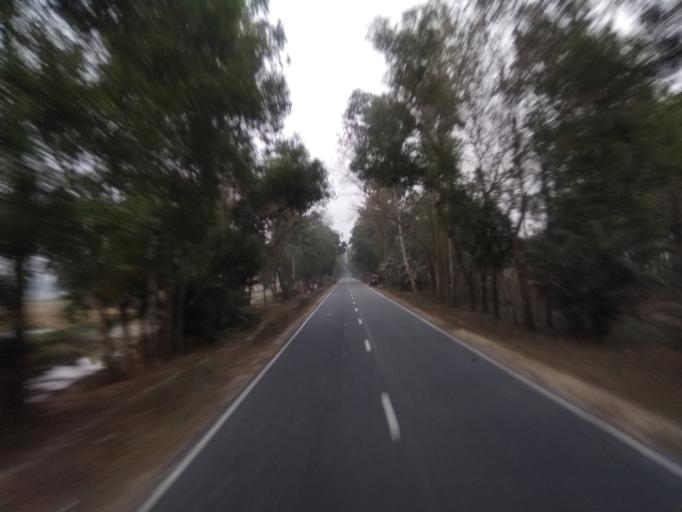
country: BD
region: Rajshahi
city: Bogra
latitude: 24.6560
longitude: 89.2633
